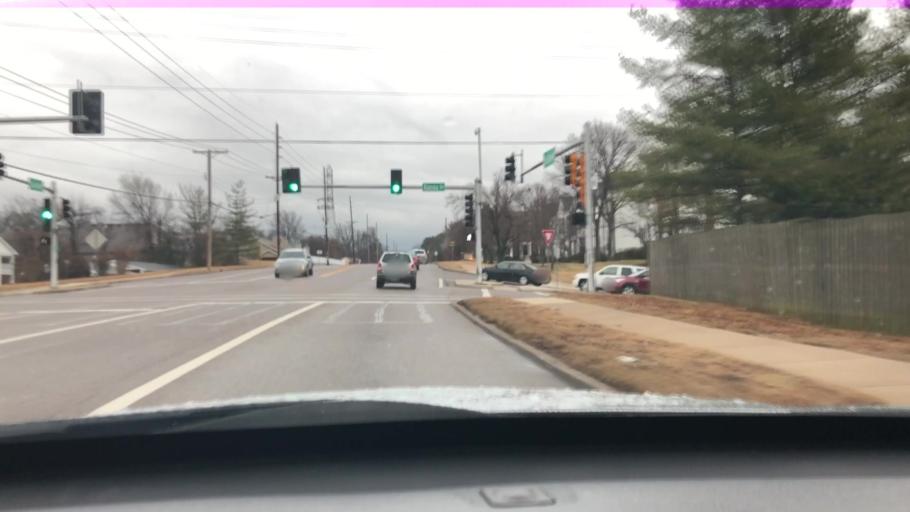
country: US
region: Missouri
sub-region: Saint Louis County
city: Valley Park
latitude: 38.5678
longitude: -90.5113
